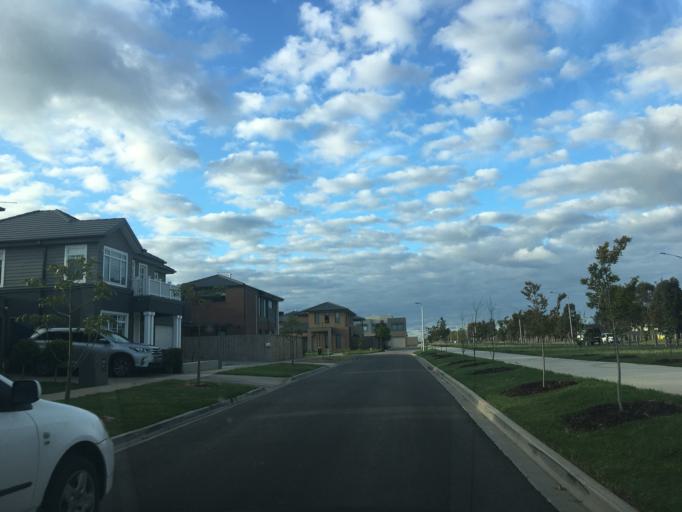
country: AU
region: Victoria
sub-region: Wyndham
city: Hoppers Crossing
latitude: -37.8913
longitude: 144.7173
